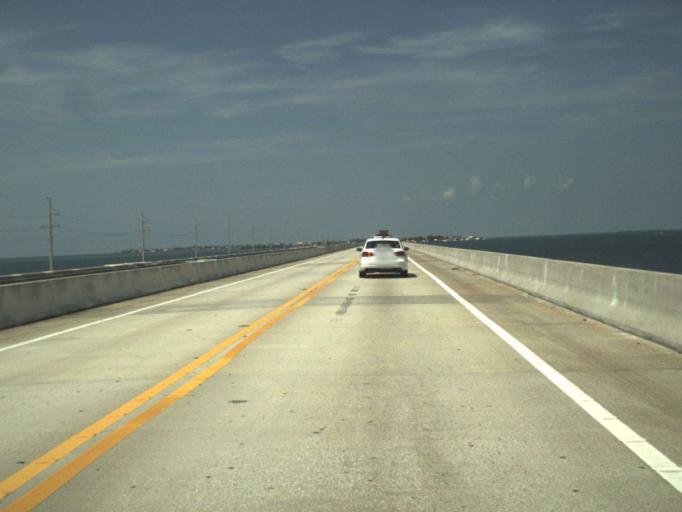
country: US
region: Florida
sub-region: Monroe County
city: Marathon
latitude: 24.7985
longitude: -80.8637
